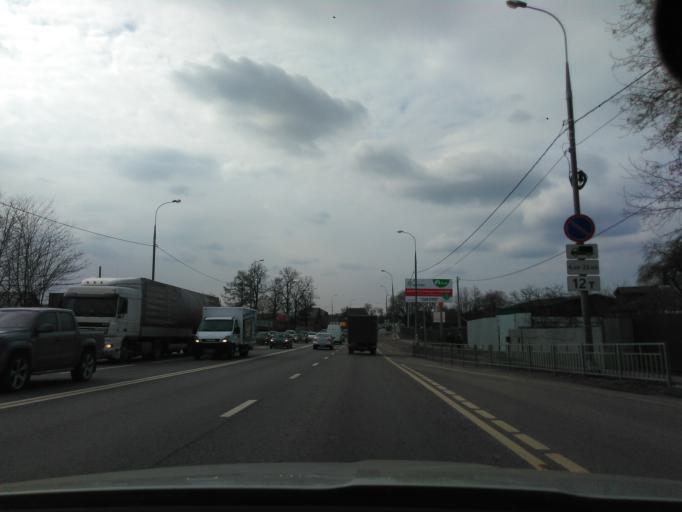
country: RU
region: Moskovskaya
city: Marfino
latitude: 56.0110
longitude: 37.5452
